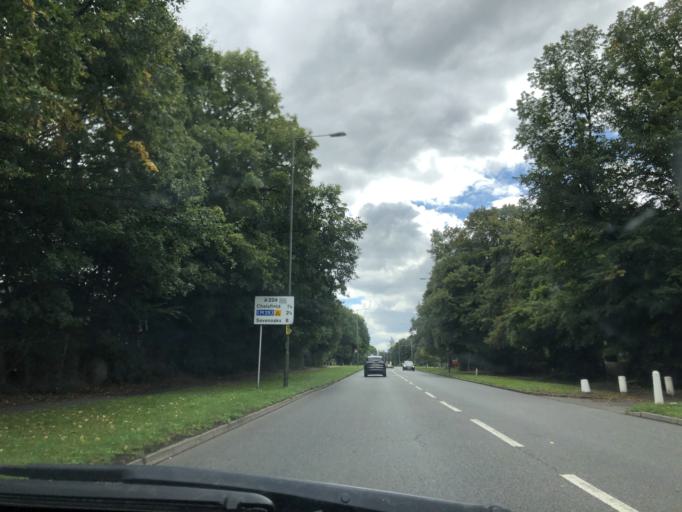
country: GB
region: England
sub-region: Greater London
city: Orpington
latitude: 51.3692
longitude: 0.1096
